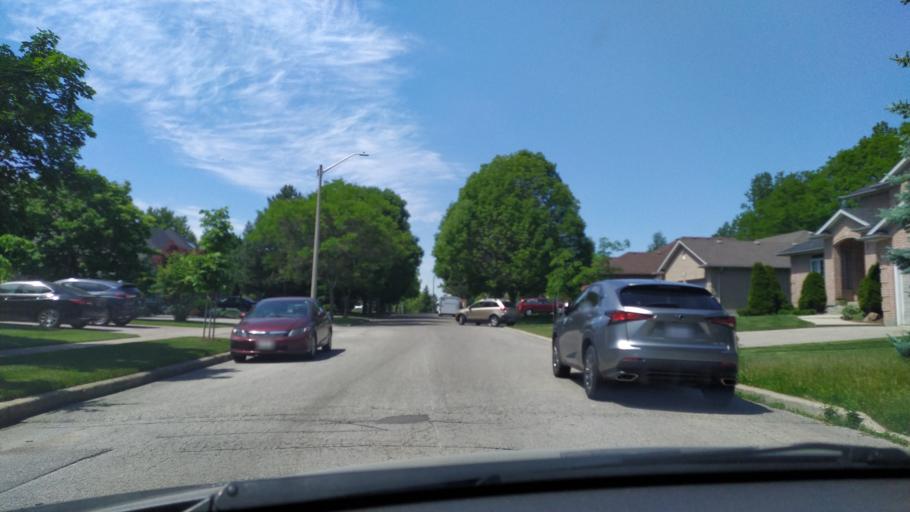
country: CA
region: Ontario
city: Waterloo
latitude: 43.4527
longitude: -80.5680
